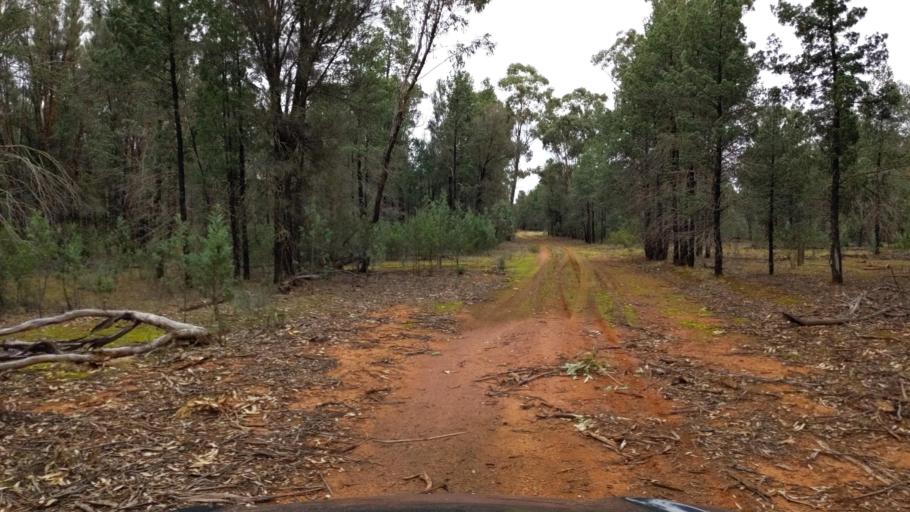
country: AU
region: New South Wales
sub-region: Coolamon
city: Coolamon
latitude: -34.8499
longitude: 146.9320
